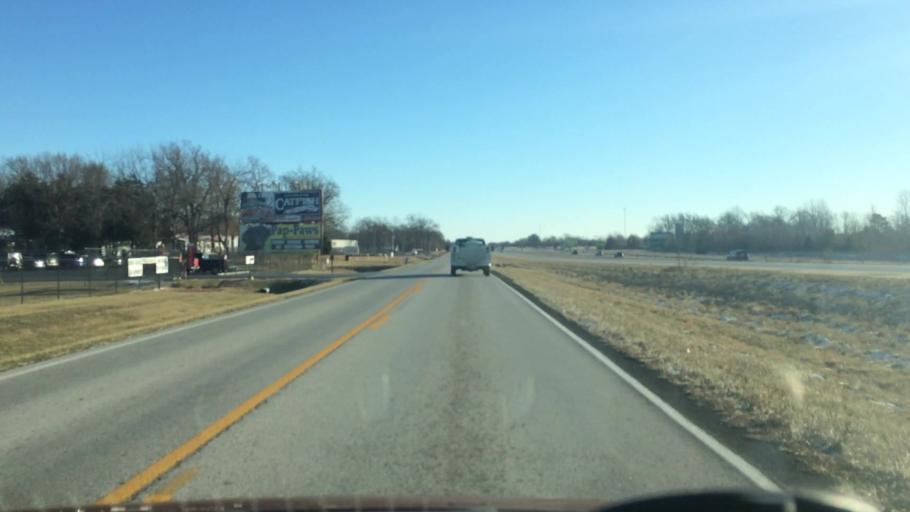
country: US
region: Missouri
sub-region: Greene County
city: Strafford
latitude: 37.2711
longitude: -93.0666
